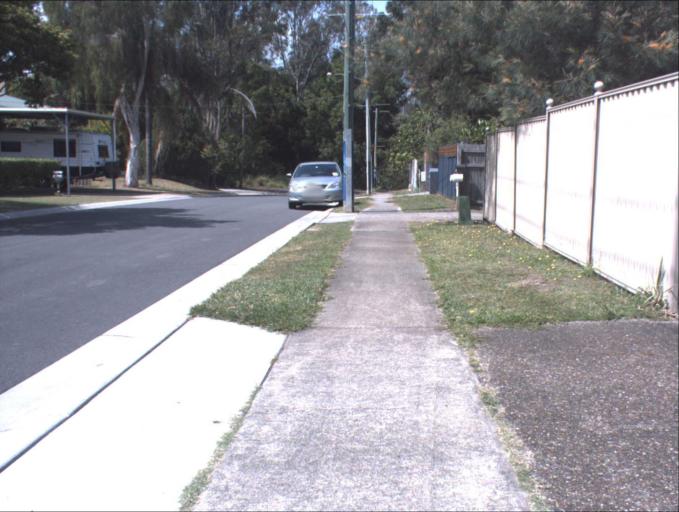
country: AU
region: Queensland
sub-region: Logan
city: Slacks Creek
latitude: -27.6464
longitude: 153.1552
